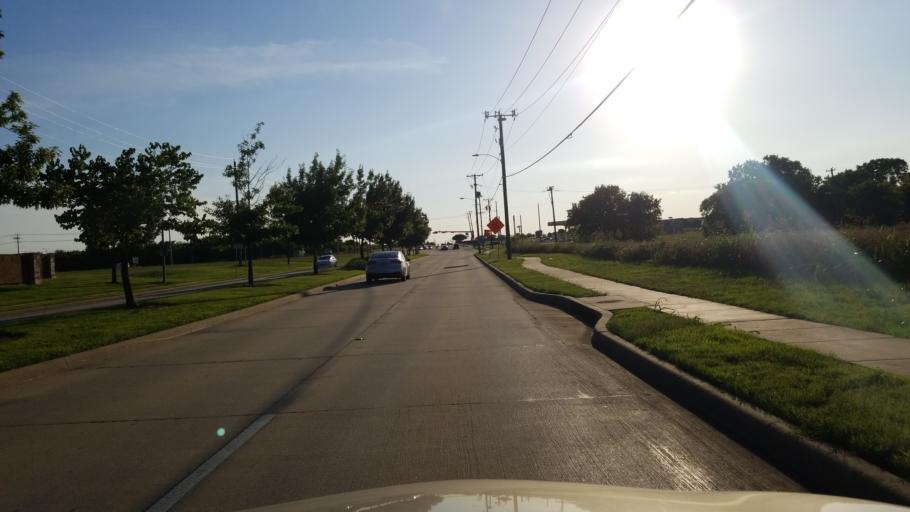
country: US
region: Texas
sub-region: Dallas County
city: Grand Prairie
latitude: 32.6914
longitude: -97.0415
